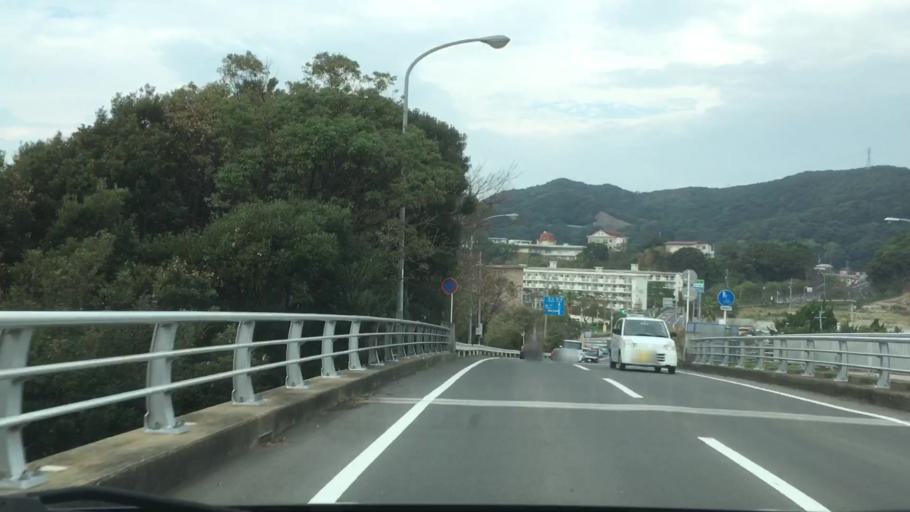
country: JP
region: Nagasaki
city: Sasebo
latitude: 33.0371
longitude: 129.6272
